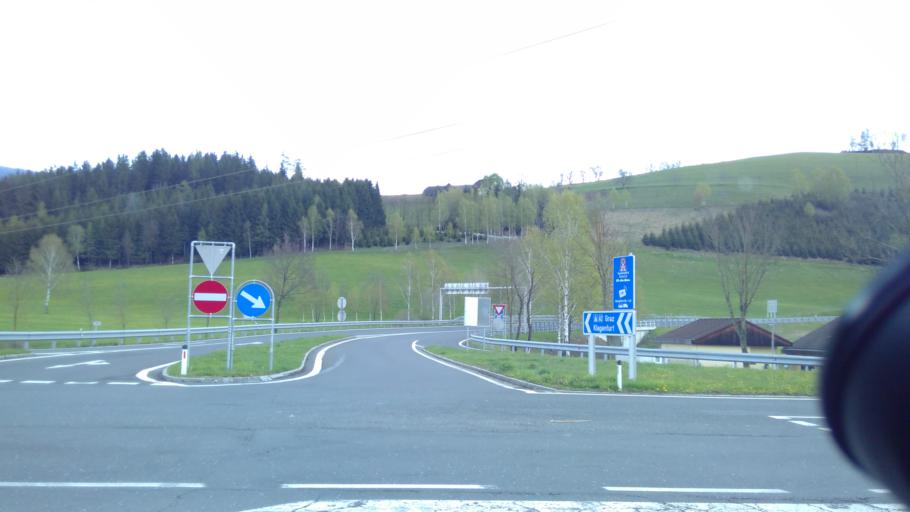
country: AT
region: Carinthia
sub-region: Politischer Bezirk Wolfsberg
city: Bad Sankt Leonhard im Lavanttal
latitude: 46.9331
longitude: 14.8278
